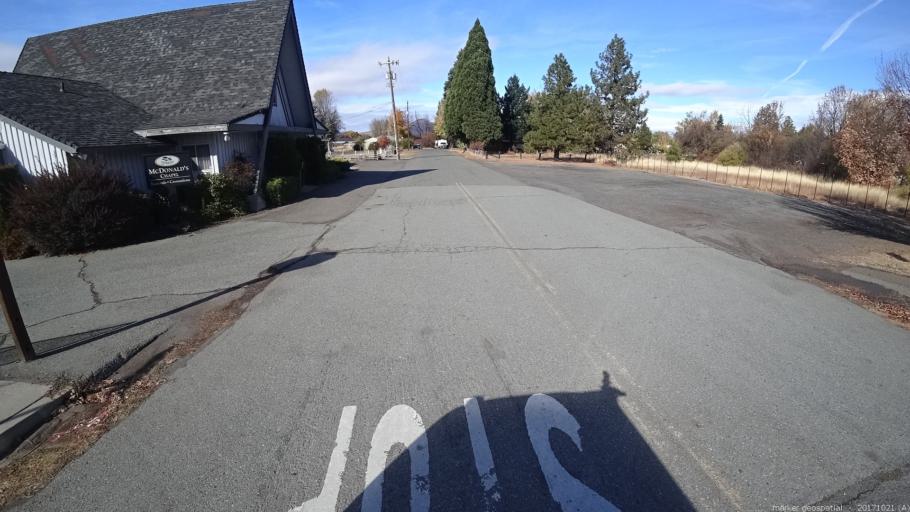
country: US
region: California
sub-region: Shasta County
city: Burney
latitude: 40.8823
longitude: -121.6632
